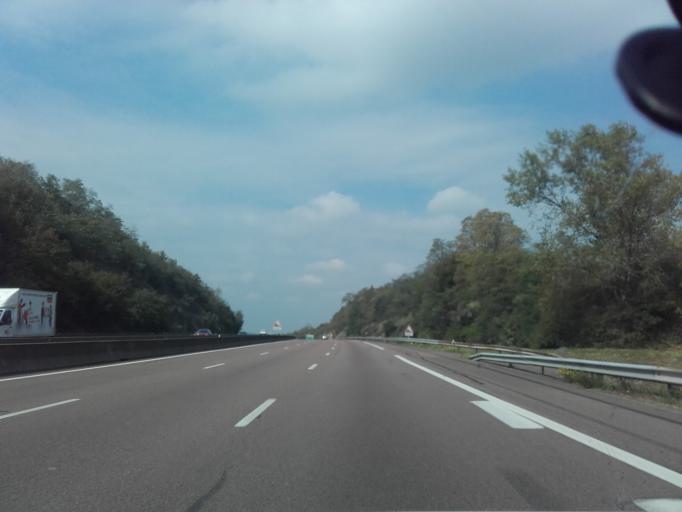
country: FR
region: Bourgogne
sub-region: Departement de Saone-et-Loire
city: Tournus
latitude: 46.5887
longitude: 4.8997
